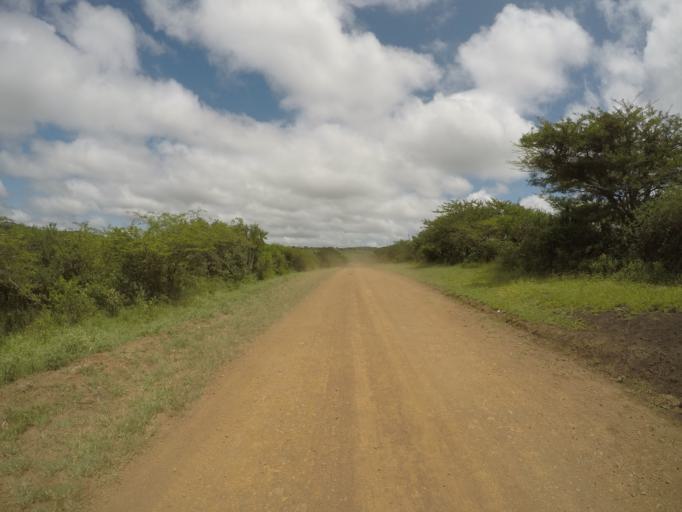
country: ZA
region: KwaZulu-Natal
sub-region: uThungulu District Municipality
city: Empangeni
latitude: -28.5688
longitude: 31.8314
